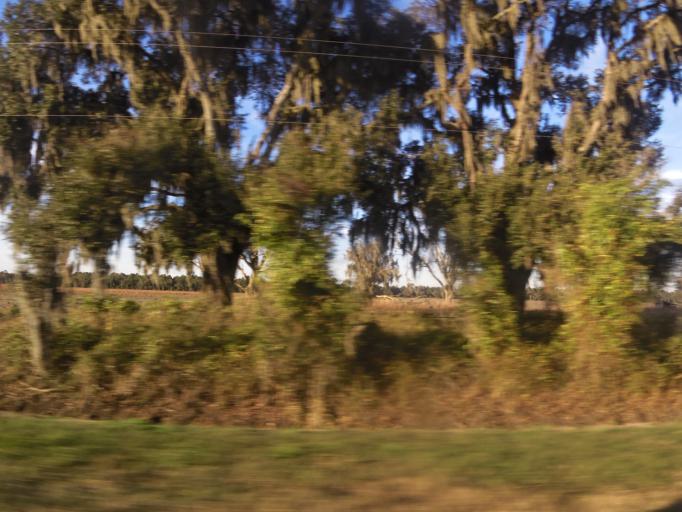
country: US
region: Florida
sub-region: Saint Johns County
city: Saint Augustine Shores
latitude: 29.7912
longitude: -81.4713
